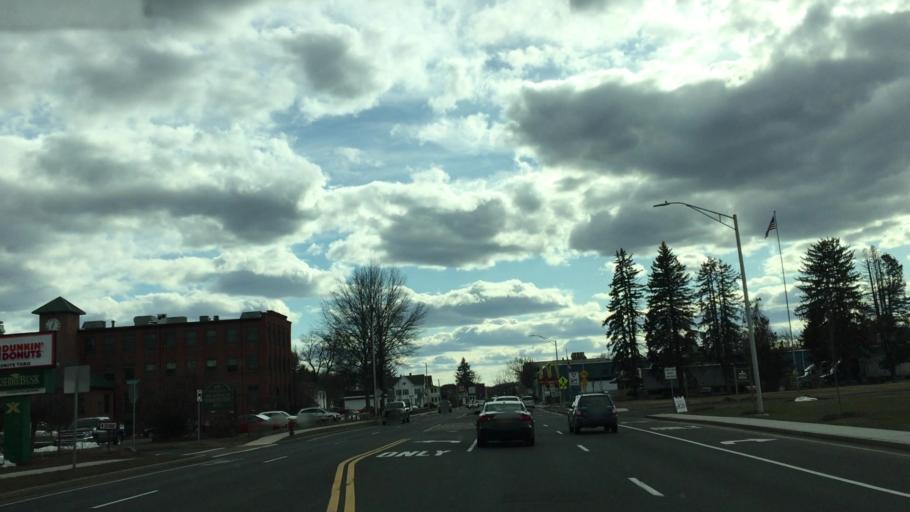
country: US
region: Massachusetts
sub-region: Hampden County
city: Westfield
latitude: 42.1352
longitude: -72.7400
